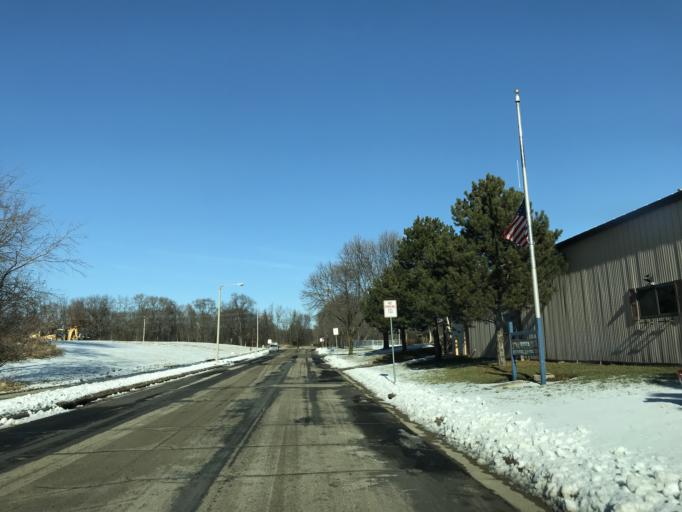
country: US
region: Wisconsin
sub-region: Dane County
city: Monona
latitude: 43.0499
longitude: -89.3168
